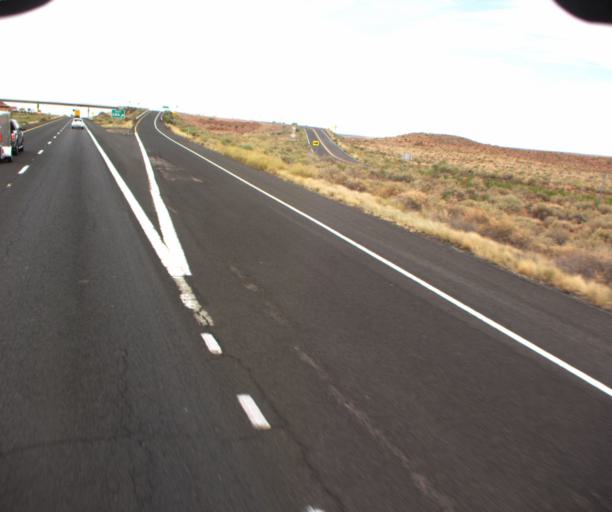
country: US
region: Arizona
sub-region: Navajo County
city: Joseph City
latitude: 34.9245
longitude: -110.2632
